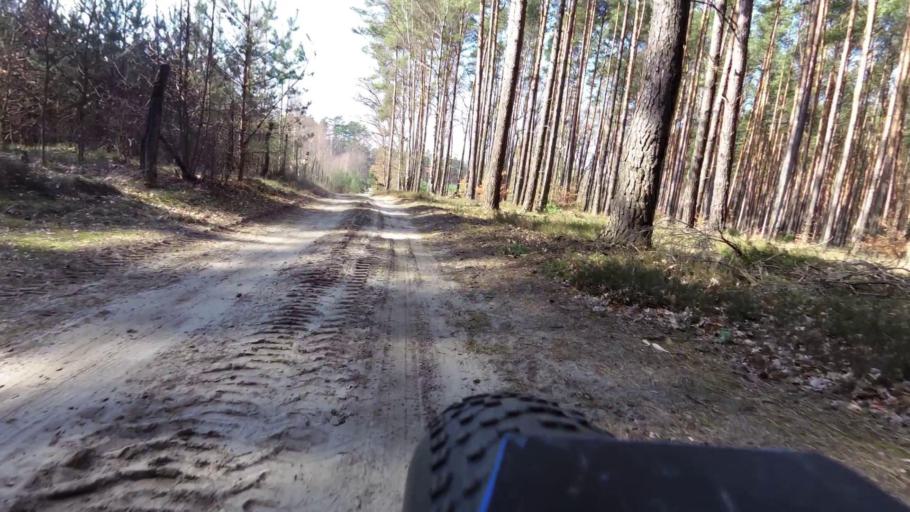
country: PL
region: Lubusz
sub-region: Powiat slubicki
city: Cybinka
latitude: 52.2035
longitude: 14.8875
